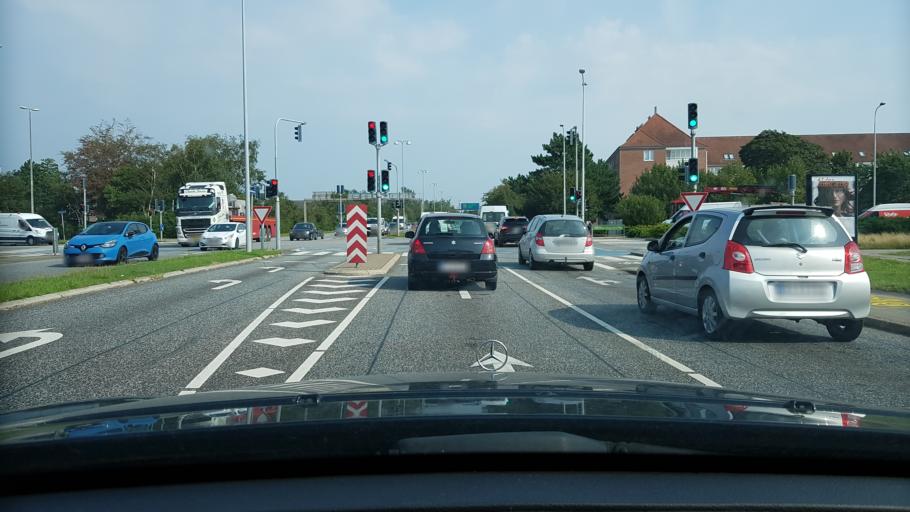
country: DK
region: North Denmark
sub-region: Alborg Kommune
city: Aalborg
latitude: 57.0699
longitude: 9.9460
